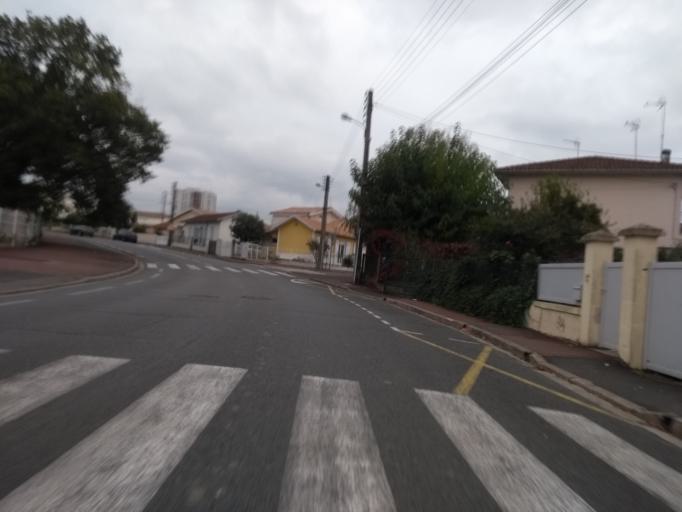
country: FR
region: Aquitaine
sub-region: Departement de la Gironde
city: Talence
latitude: 44.7999
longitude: -0.5934
